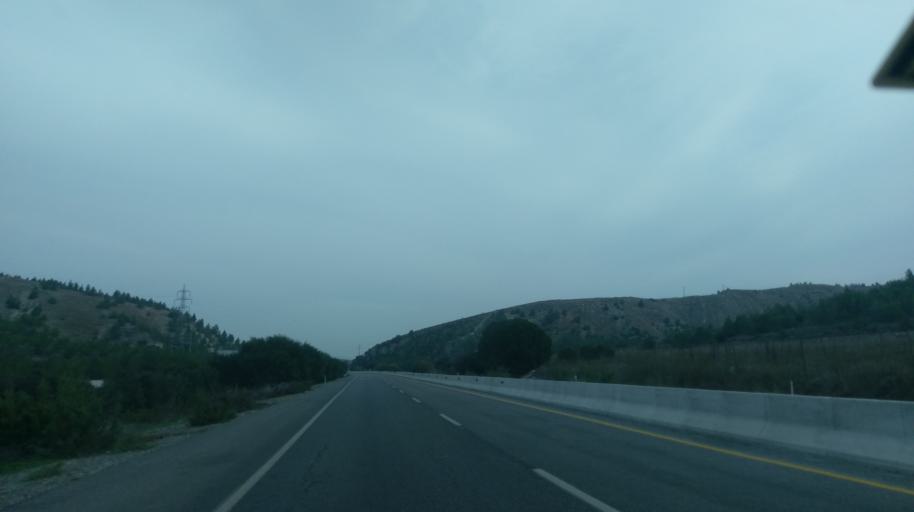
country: CY
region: Lefkosia
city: Akaki
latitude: 35.2078
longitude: 33.1213
